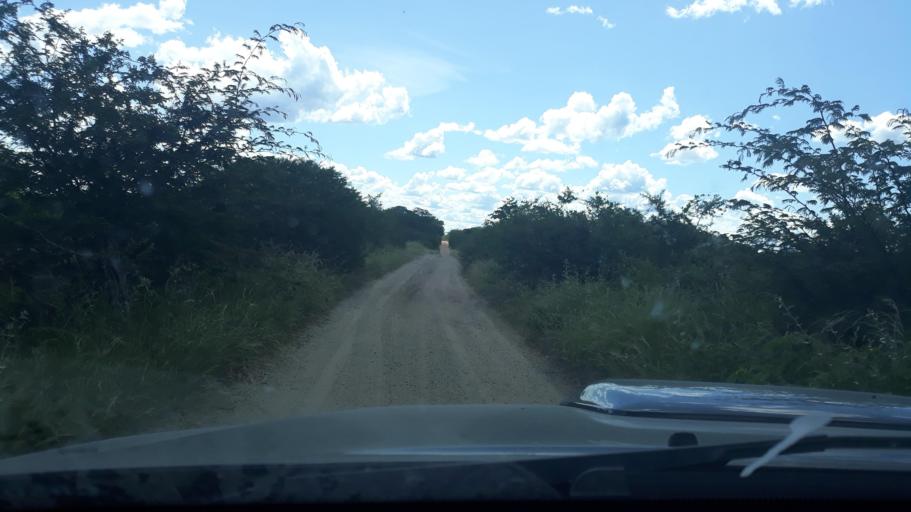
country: BR
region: Bahia
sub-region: Riacho De Santana
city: Riacho de Santana
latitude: -13.8595
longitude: -43.0362
